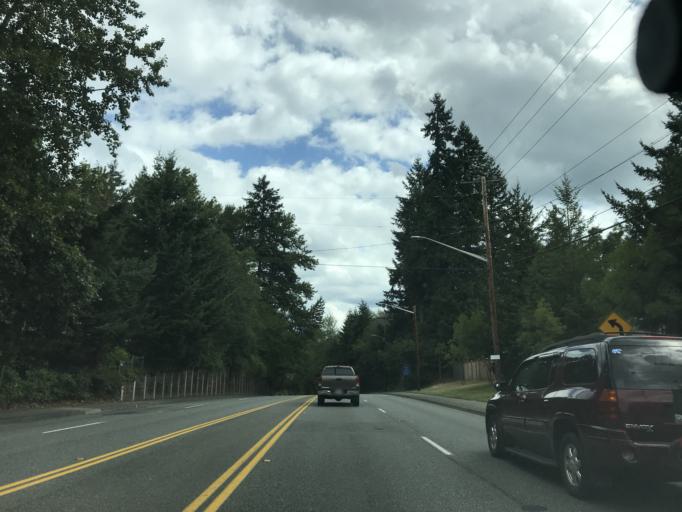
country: US
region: Washington
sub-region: King County
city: Fairwood
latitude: 47.4459
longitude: -122.1691
